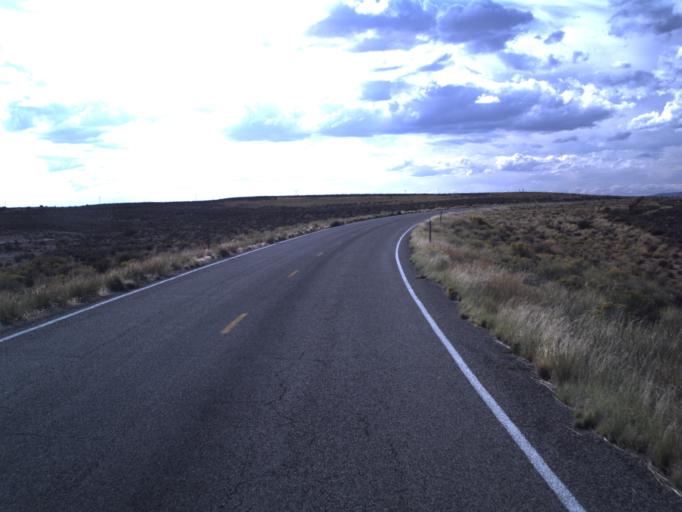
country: US
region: Utah
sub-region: San Juan County
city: Blanding
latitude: 37.3249
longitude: -109.3395
